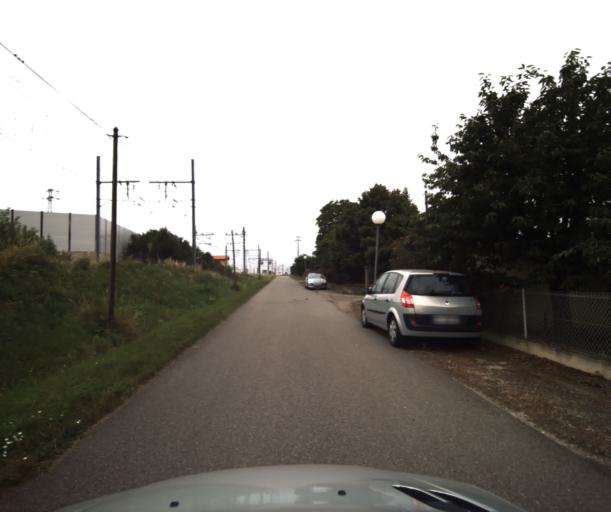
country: FR
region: Midi-Pyrenees
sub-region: Departement de la Haute-Garonne
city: Pinsaguel
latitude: 43.5164
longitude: 1.3854
